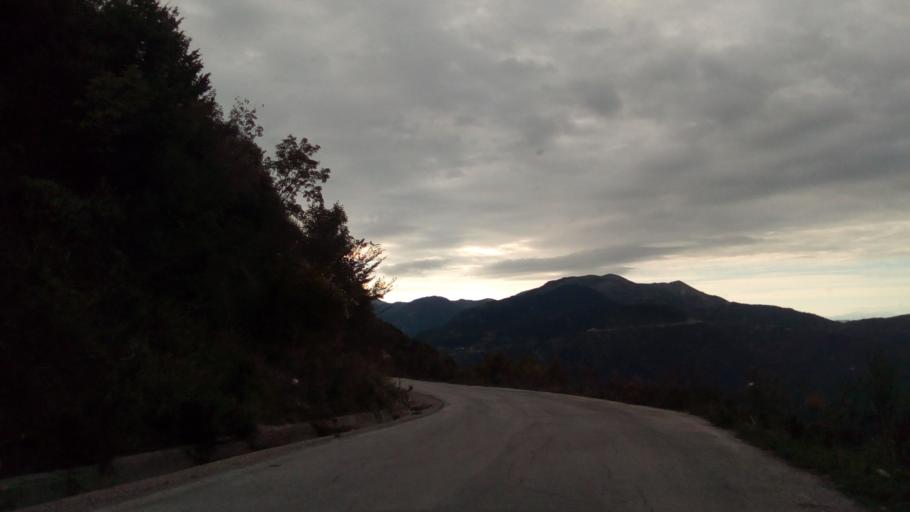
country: GR
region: West Greece
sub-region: Nomos Aitolias kai Akarnanias
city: Thermo
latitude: 38.6056
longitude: 21.8012
